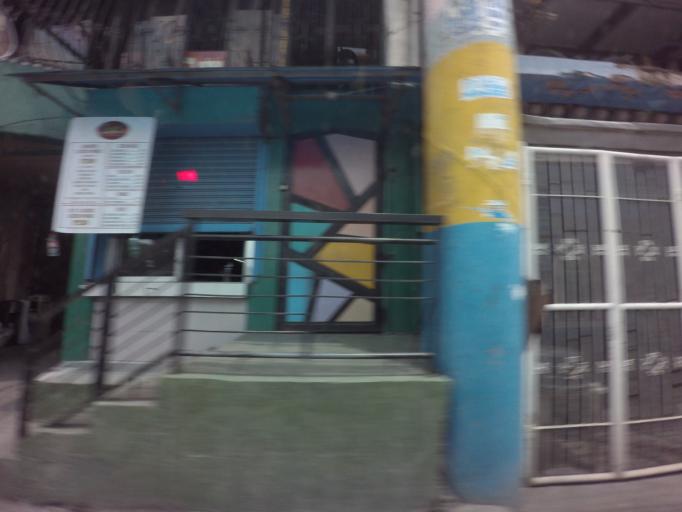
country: PH
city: Sambayanihan People's Village
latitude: 14.4356
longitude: 121.0501
